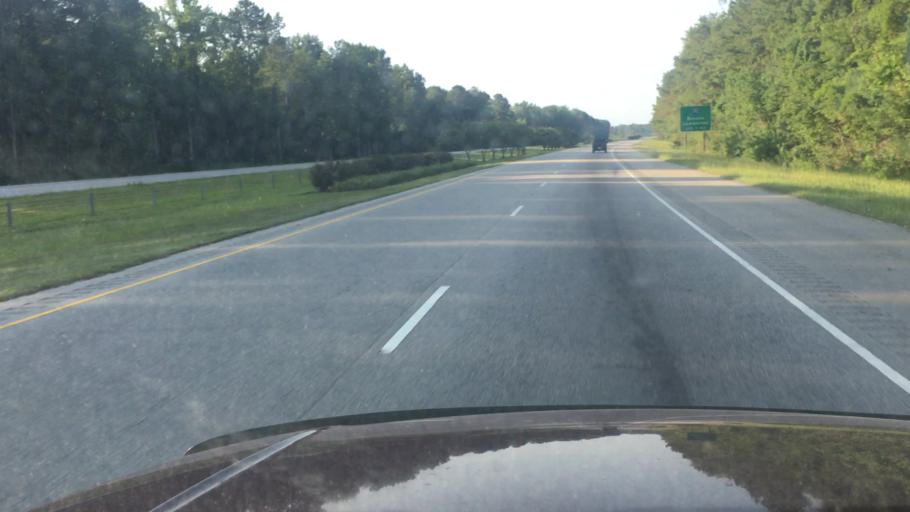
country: US
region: North Carolina
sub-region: Cumberland County
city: Fayetteville
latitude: 34.9955
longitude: -78.8631
